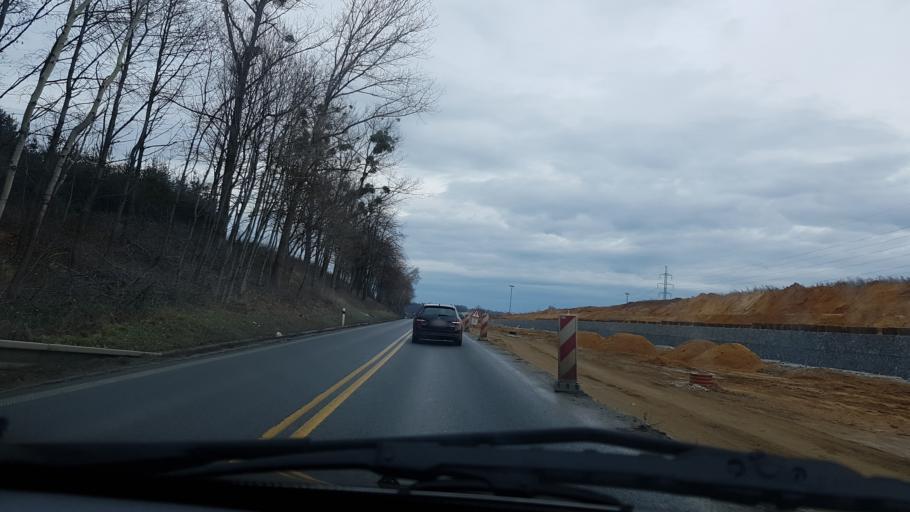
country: CZ
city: Rybi
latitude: 49.6243
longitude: 18.0789
